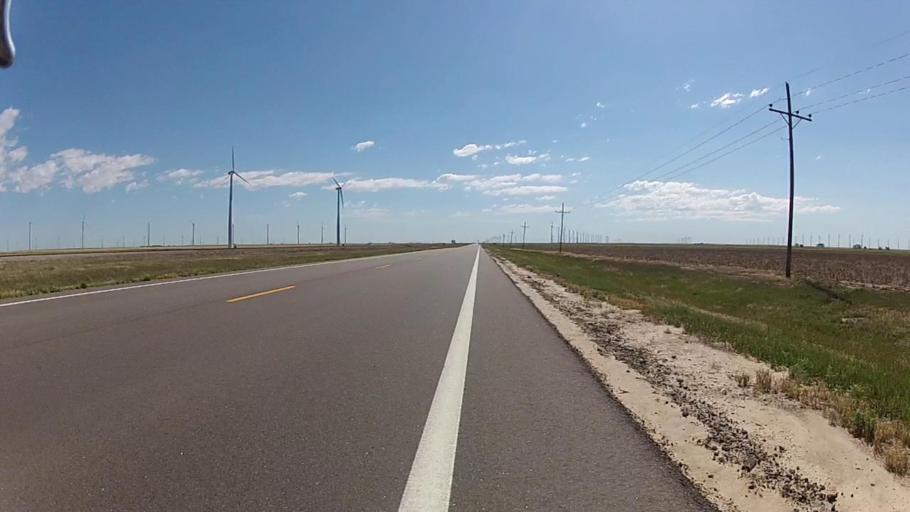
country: US
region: Kansas
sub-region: Gray County
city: Cimarron
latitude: 37.6104
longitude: -100.4032
